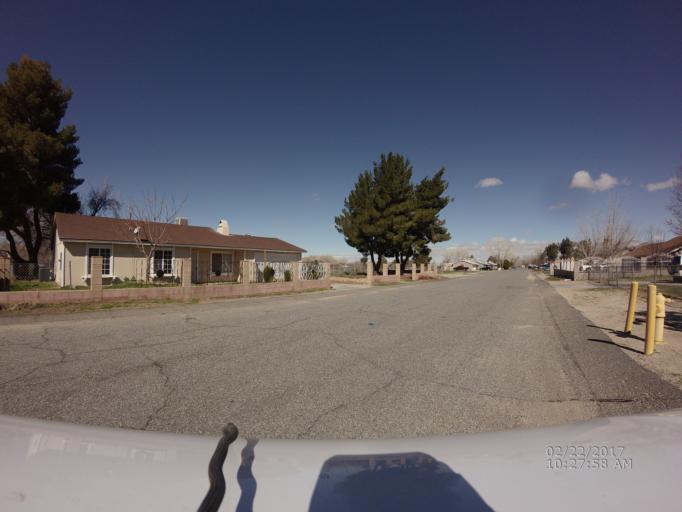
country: US
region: California
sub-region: Los Angeles County
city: Lake Los Angeles
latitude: 34.6278
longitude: -117.8193
